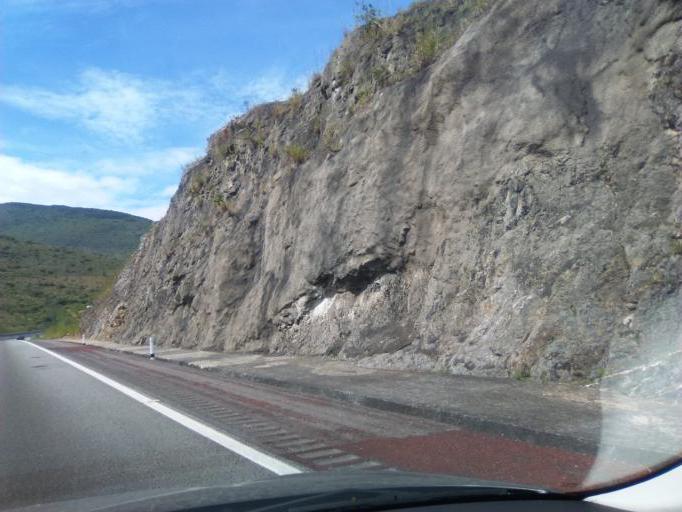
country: MX
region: Guerrero
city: Mazatlan
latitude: 17.4296
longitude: -99.4736
